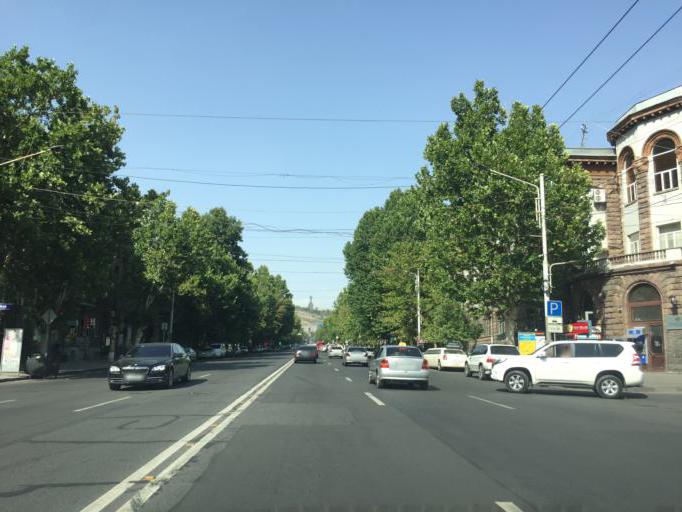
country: AM
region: Yerevan
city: Yerevan
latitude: 40.1822
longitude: 44.5093
